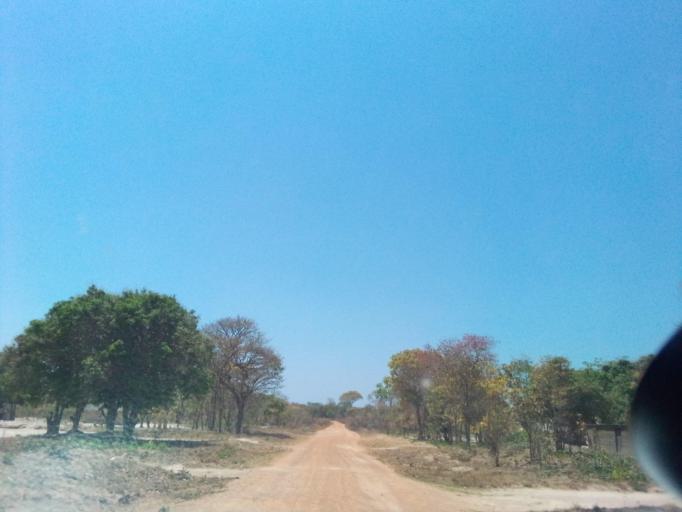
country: ZM
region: Northern
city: Mpika
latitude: -12.2527
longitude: 30.6766
